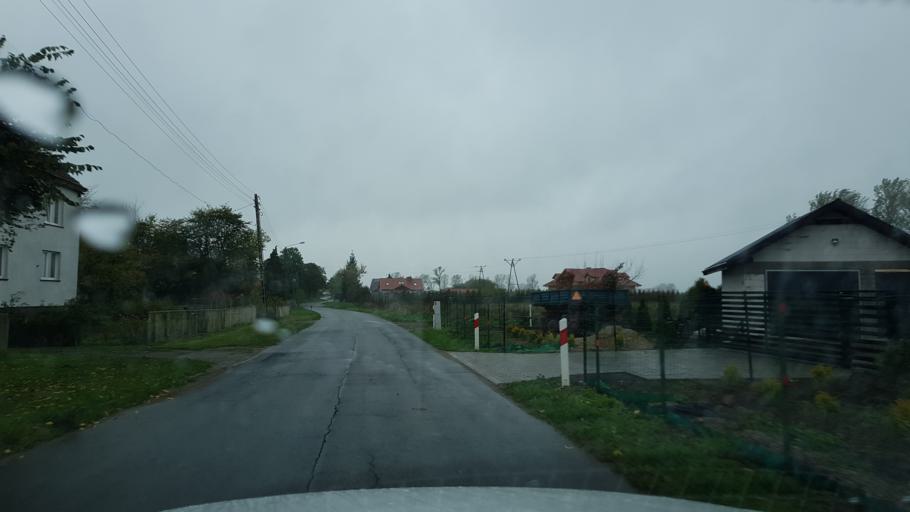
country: PL
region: West Pomeranian Voivodeship
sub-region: Powiat pyrzycki
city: Pyrzyce
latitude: 53.1607
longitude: 14.8424
